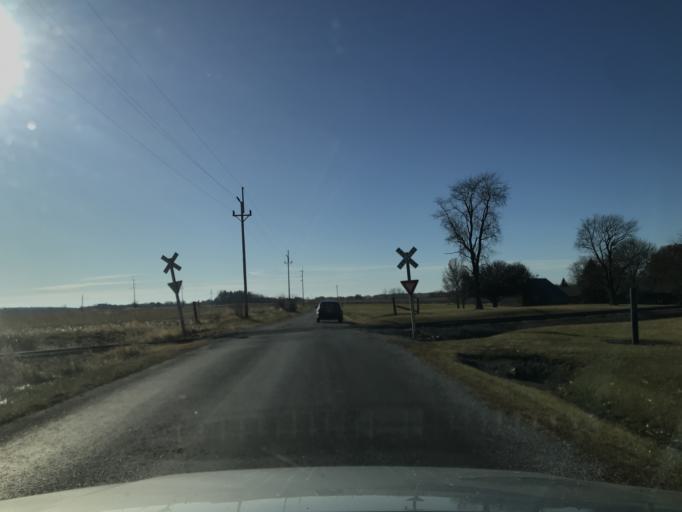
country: US
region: Illinois
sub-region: Hancock County
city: Carthage
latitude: 40.4637
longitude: -91.1784
